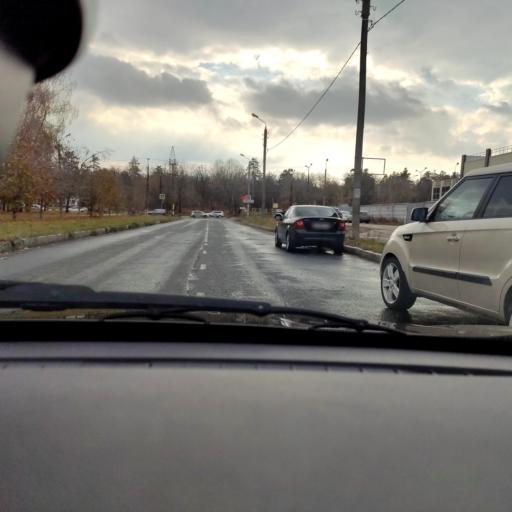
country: RU
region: Samara
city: Tol'yatti
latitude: 53.4998
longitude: 49.4016
